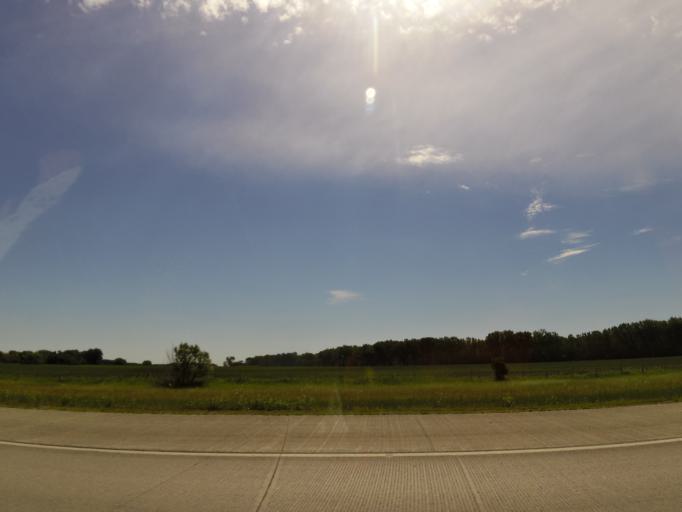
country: US
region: North Dakota
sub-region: Traill County
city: Hillsboro
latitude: 47.5477
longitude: -97.0826
